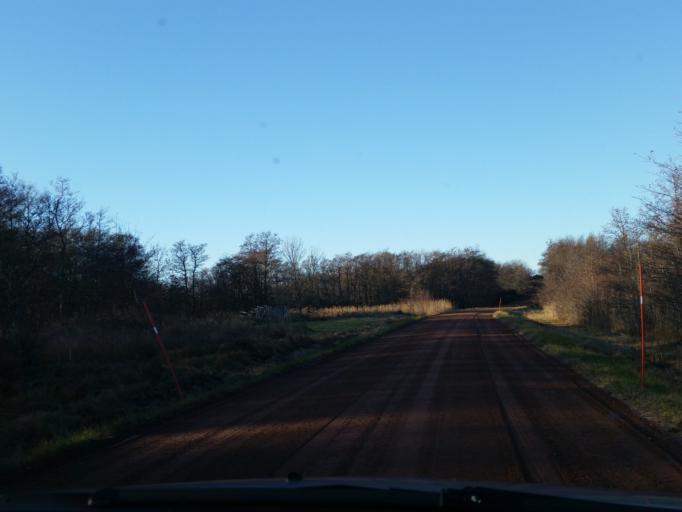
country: AX
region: Alands skaergard
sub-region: Braendoe
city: Braendoe
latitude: 60.4203
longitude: 20.9778
